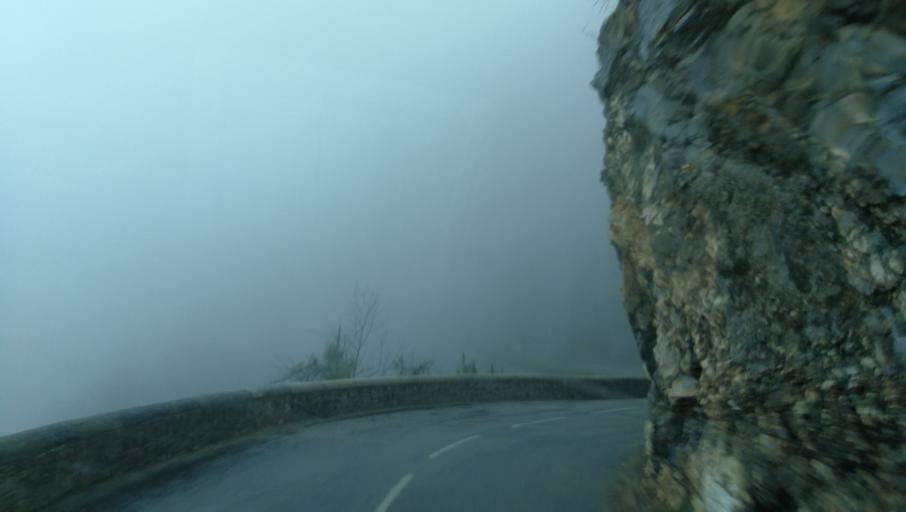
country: FR
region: Rhone-Alpes
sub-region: Departement de la Drome
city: Saint-Laurent-en-Royans
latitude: 44.9806
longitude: 5.3331
